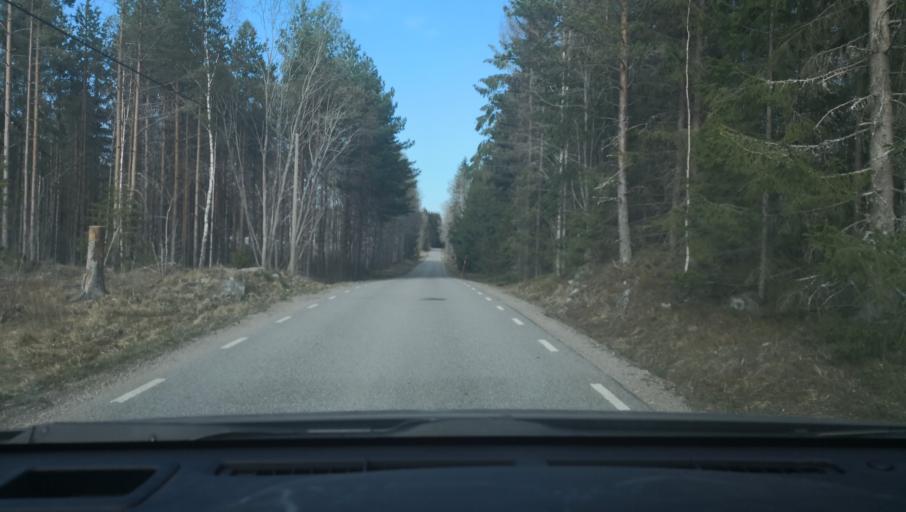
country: SE
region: Uppsala
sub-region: Heby Kommun
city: Heby
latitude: 59.9185
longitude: 16.8408
